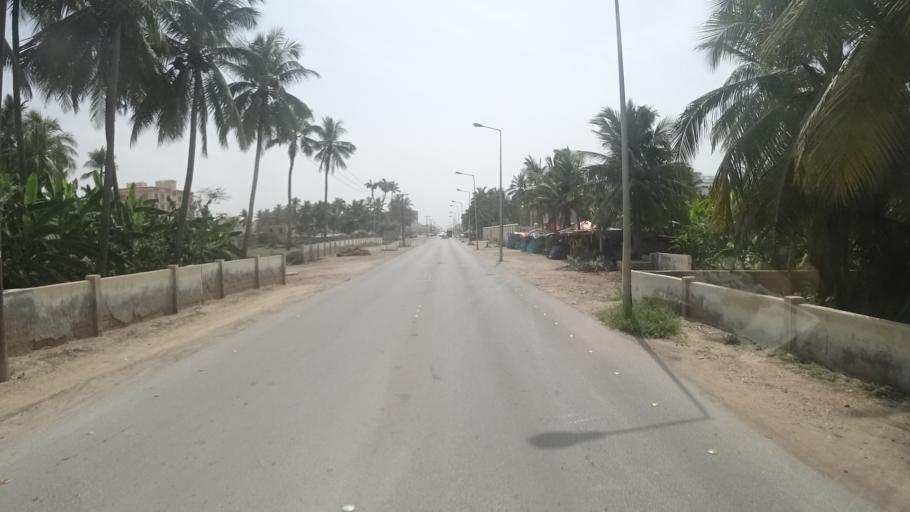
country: OM
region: Zufar
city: Salalah
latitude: 17.0176
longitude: 54.1565
